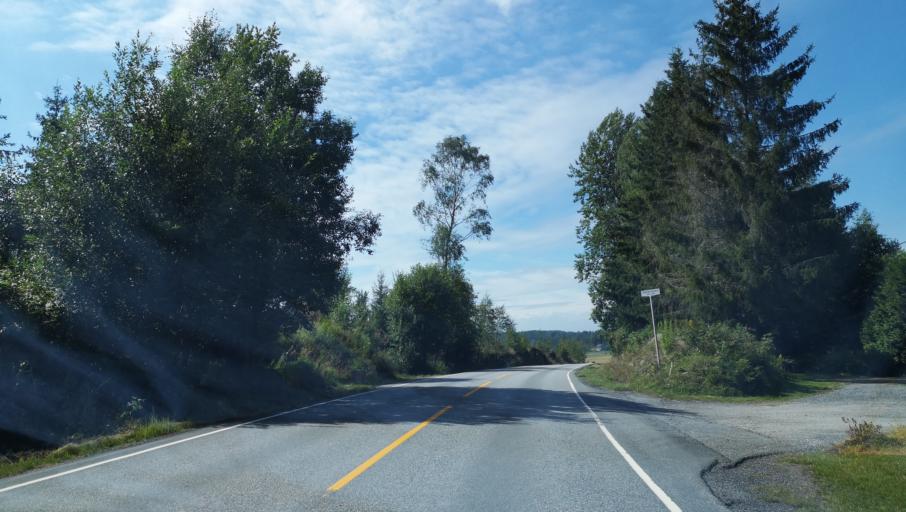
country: NO
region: Ostfold
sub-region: Valer
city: Kirkebygda
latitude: 59.5525
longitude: 10.8242
